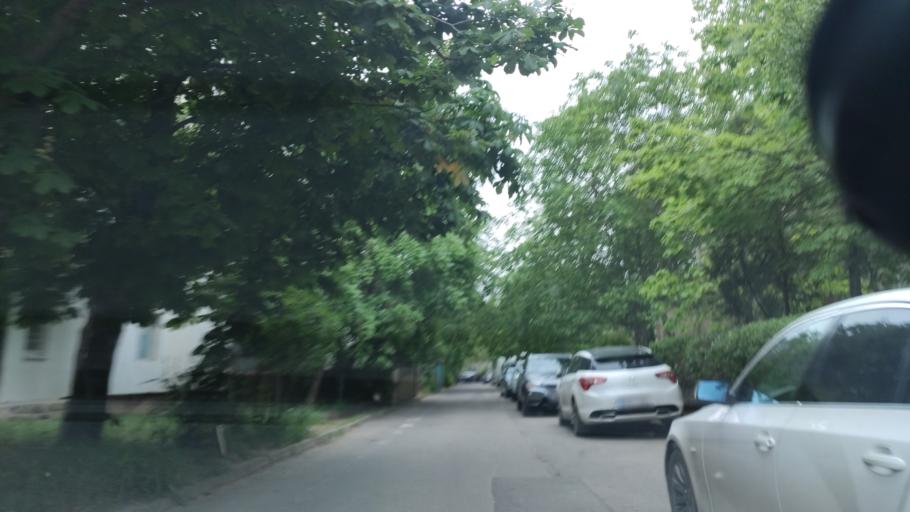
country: MD
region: Chisinau
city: Chisinau
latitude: 46.9828
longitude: 28.8684
